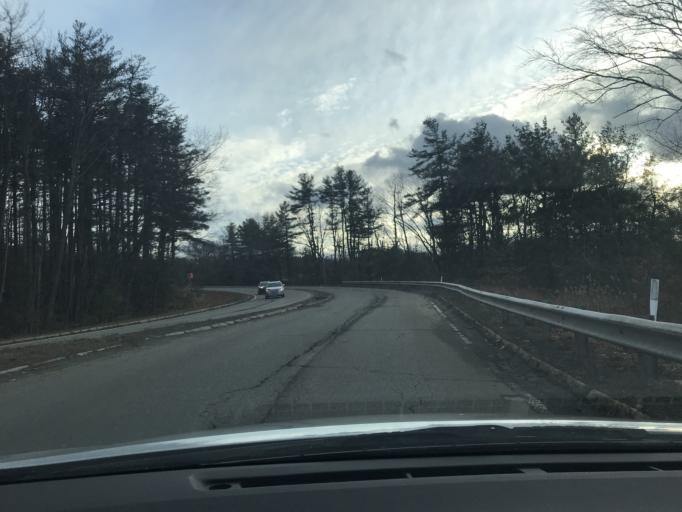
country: US
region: Massachusetts
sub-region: Middlesex County
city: Littleton Common
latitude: 42.5212
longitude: -71.5109
